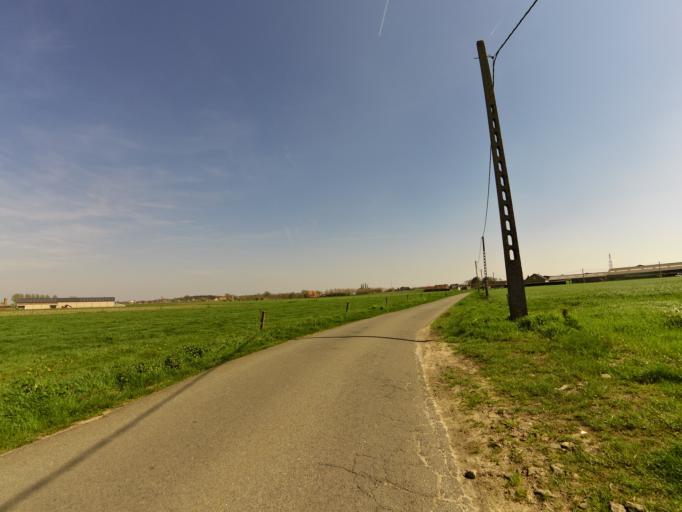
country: BE
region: Flanders
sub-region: Provincie West-Vlaanderen
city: Ichtegem
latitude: 51.0765
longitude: 3.0086
